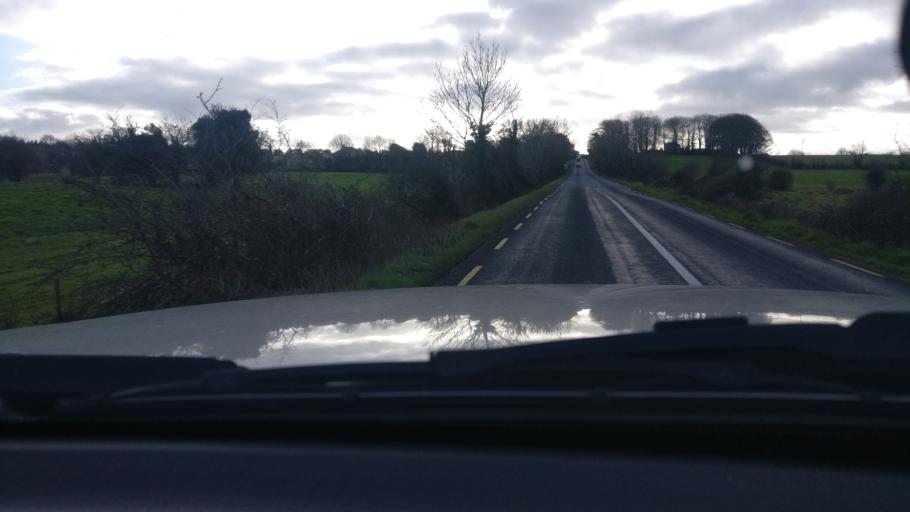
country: IE
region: Connaught
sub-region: County Galway
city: Ballinasloe
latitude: 53.3081
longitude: -8.2429
